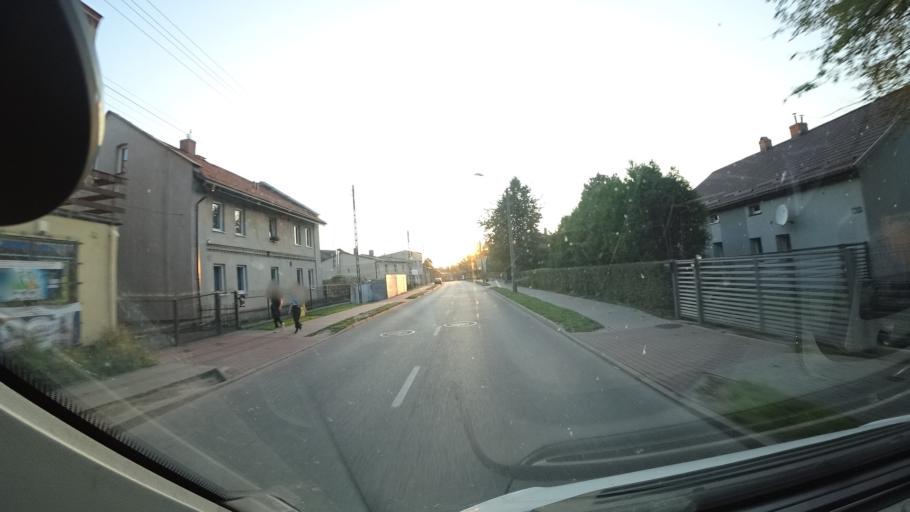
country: PL
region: Silesian Voivodeship
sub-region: Zabrze
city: Zabrze
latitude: 50.2807
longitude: 18.8059
